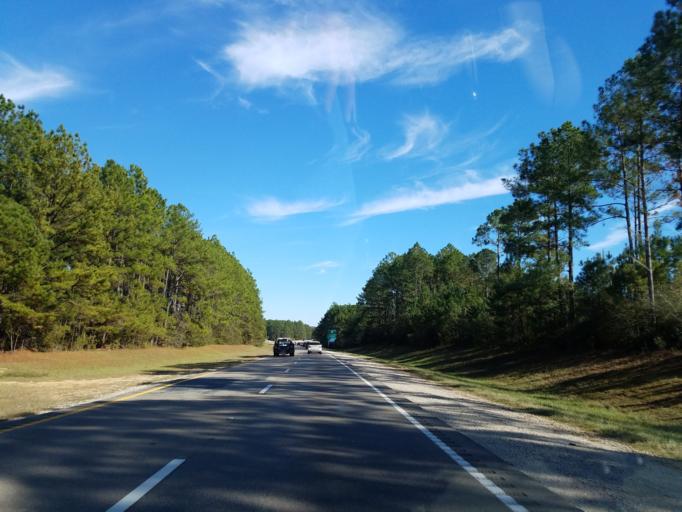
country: US
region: Mississippi
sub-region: Forrest County
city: Hattiesburg
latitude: 31.2426
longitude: -89.2854
